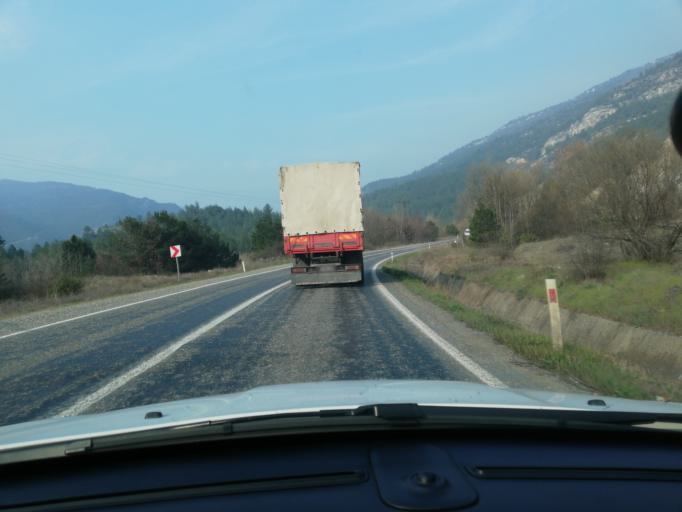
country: TR
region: Karabuk
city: Karabuk
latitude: 41.1662
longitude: 32.5771
